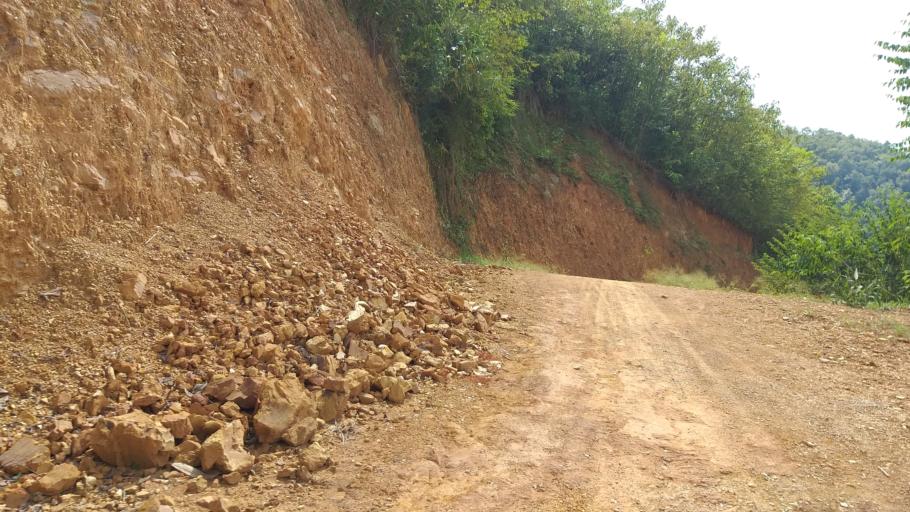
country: LA
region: Phongsali
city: Khoa
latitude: 21.2734
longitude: 102.5225
